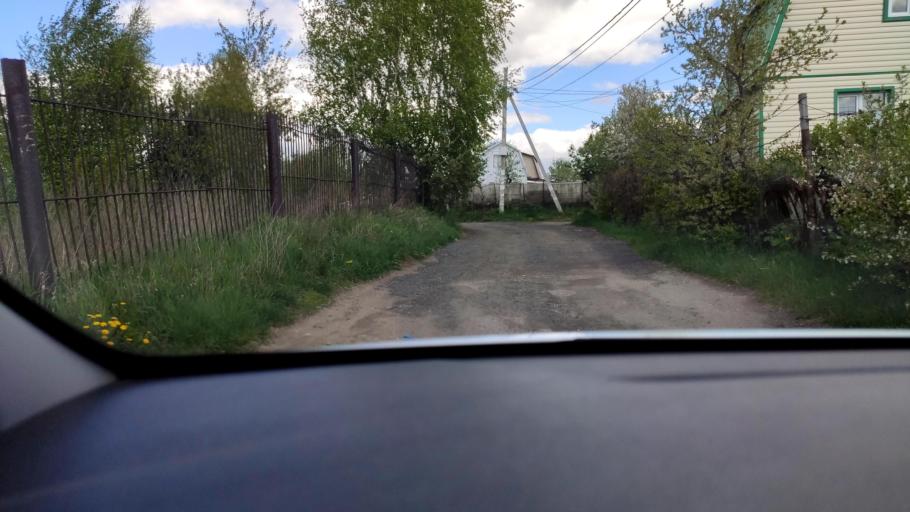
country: RU
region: Tatarstan
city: Stolbishchi
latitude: 55.7042
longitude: 49.1561
